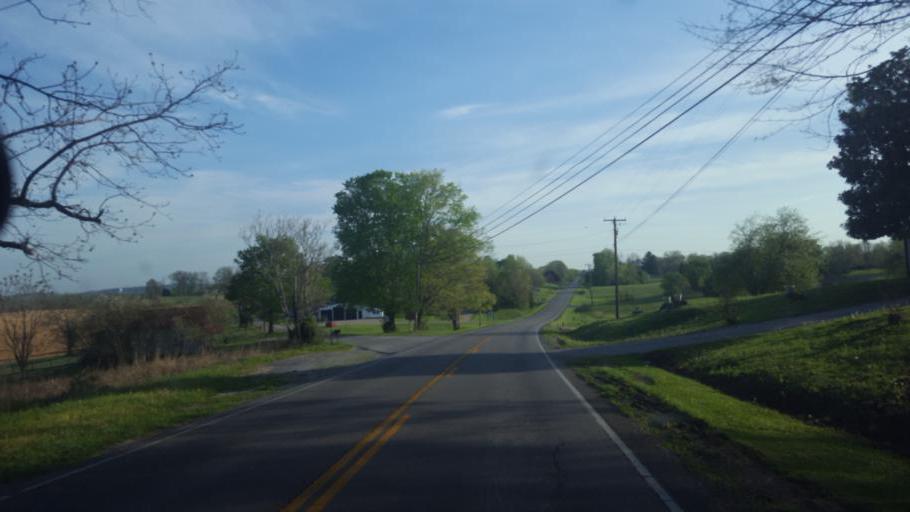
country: US
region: Kentucky
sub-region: Hart County
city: Munfordville
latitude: 37.2527
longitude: -85.8881
